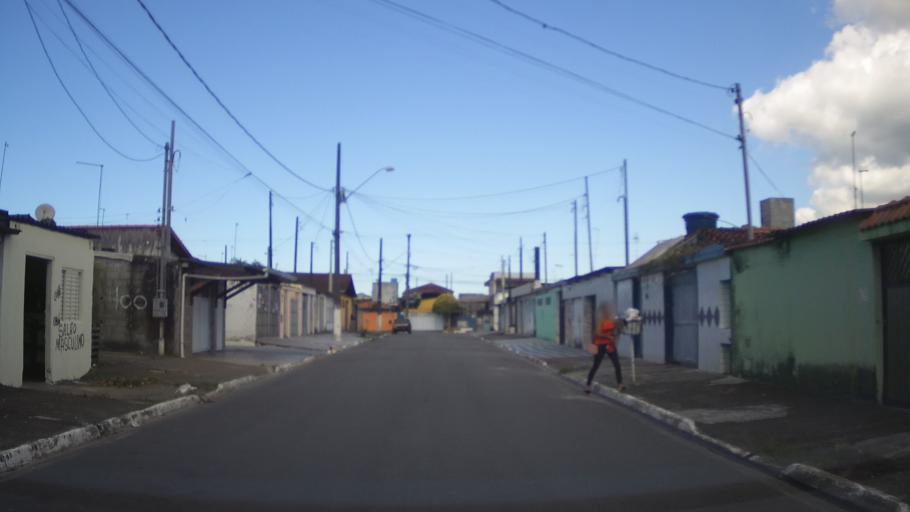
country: BR
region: Sao Paulo
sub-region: Praia Grande
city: Praia Grande
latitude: -24.0284
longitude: -46.5085
